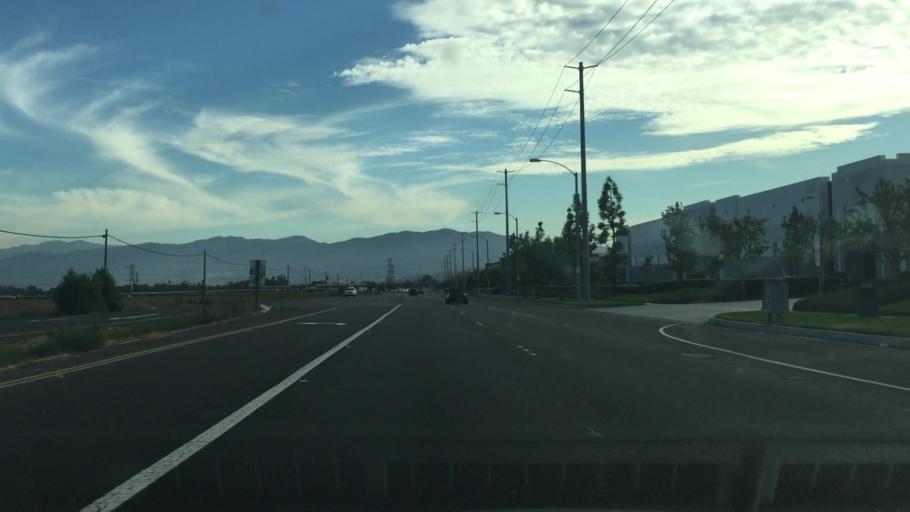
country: US
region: California
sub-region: San Bernardino County
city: Los Serranos
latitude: 33.9663
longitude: -117.6508
